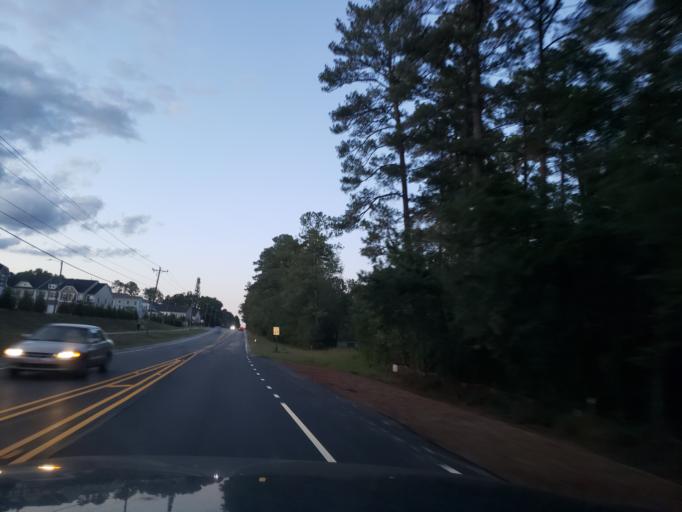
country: US
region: North Carolina
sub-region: Orange County
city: Chapel Hill
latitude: 35.8886
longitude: -78.9573
